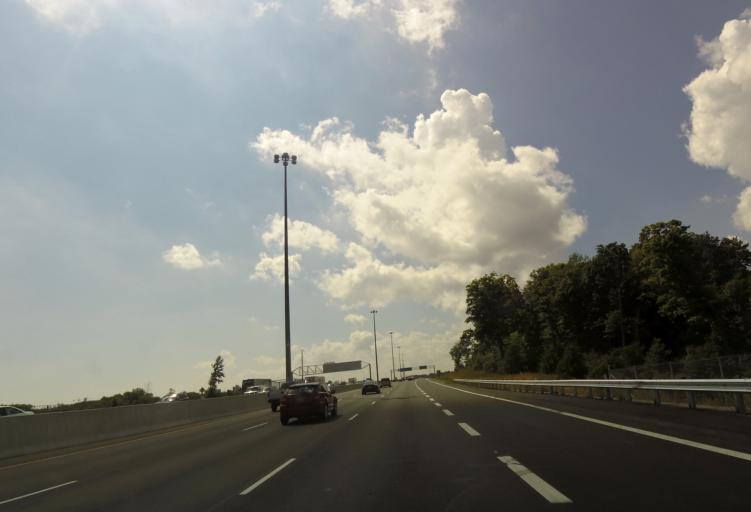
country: CA
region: Ontario
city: Ajax
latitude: 43.8574
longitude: -79.0033
